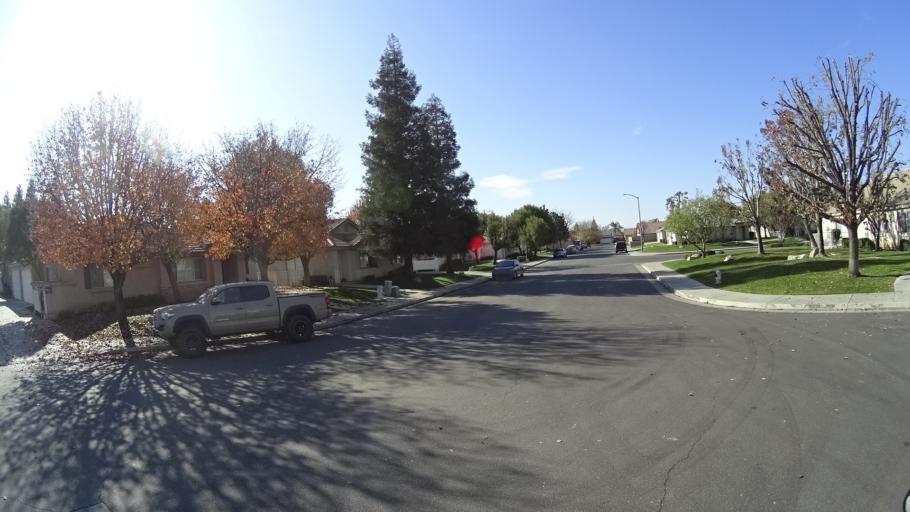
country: US
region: California
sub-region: Kern County
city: Greenacres
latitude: 35.3985
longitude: -119.0928
